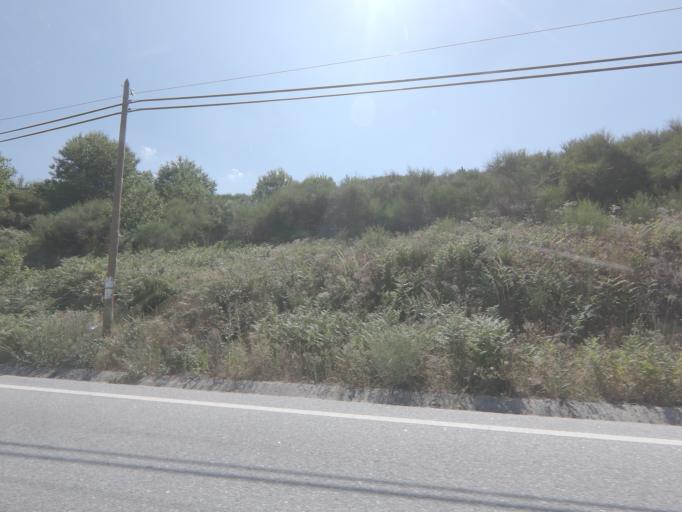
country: PT
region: Viseu
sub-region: Tarouca
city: Tarouca
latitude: 41.0082
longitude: -7.7835
